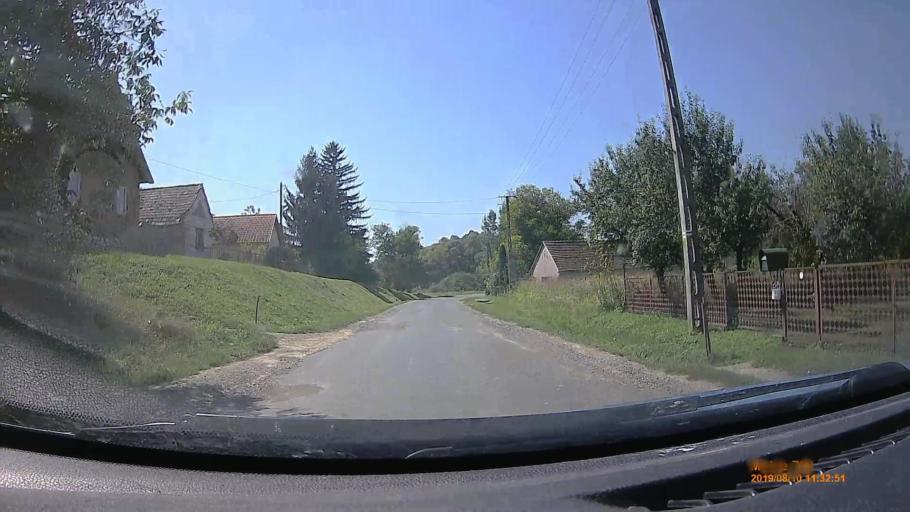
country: HU
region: Somogy
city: Somogyvar
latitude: 46.5248
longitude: 17.7877
